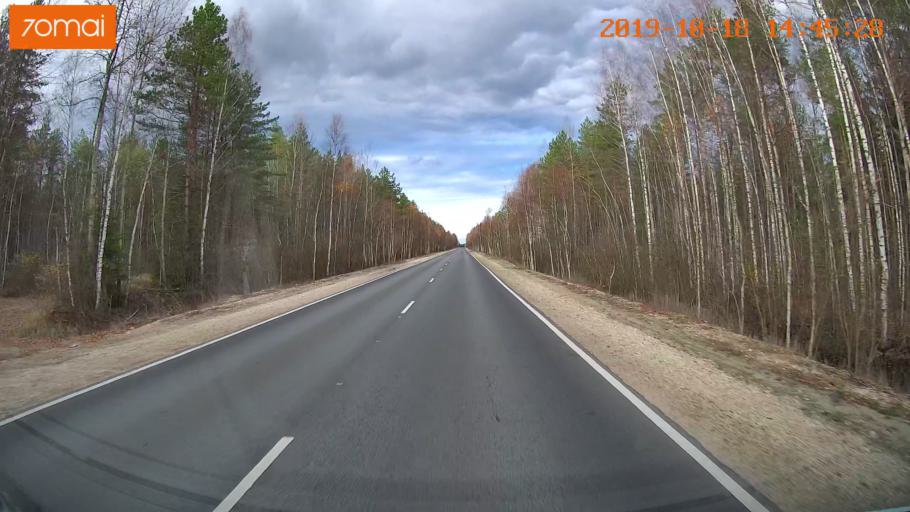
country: RU
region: Vladimir
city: Velikodvorskiy
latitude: 55.3555
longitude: 40.6790
